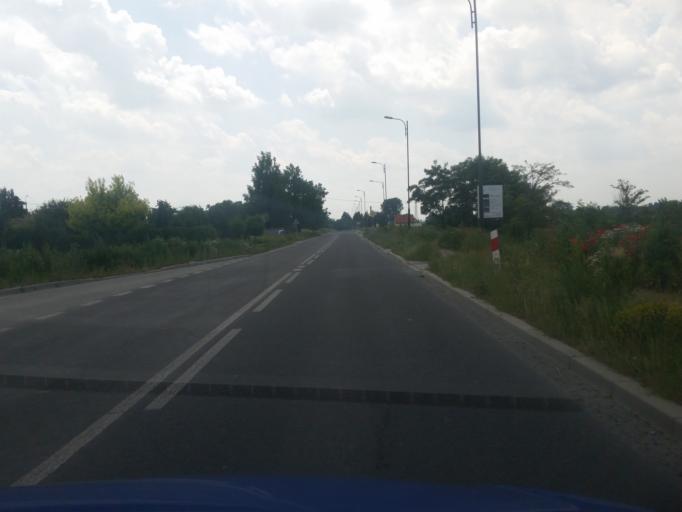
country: PL
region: Swietokrzyskie
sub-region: Powiat buski
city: Busko-Zdroj
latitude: 50.4482
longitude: 20.7110
